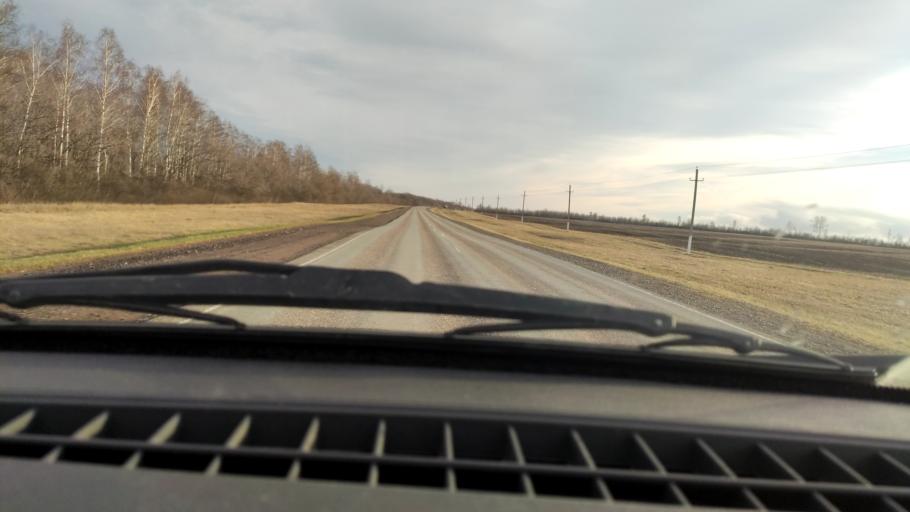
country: RU
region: Bashkortostan
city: Davlekanovo
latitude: 54.3339
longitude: 55.1682
